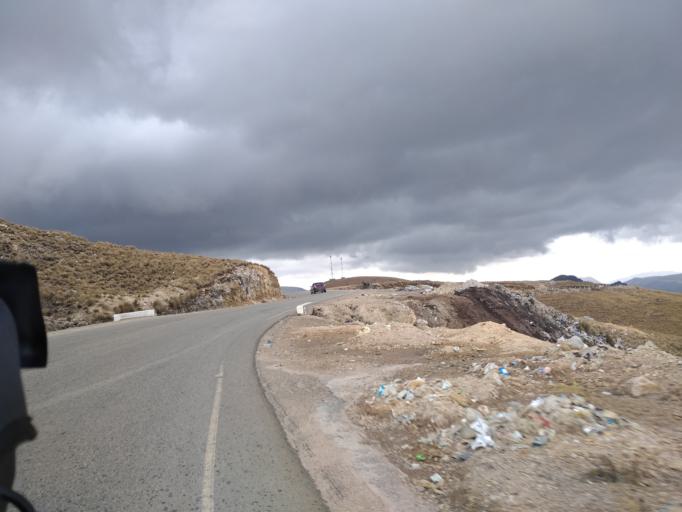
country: PE
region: La Libertad
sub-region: Provincia de Santiago de Chuco
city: Quiruvilca
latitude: -7.9931
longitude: -78.3033
